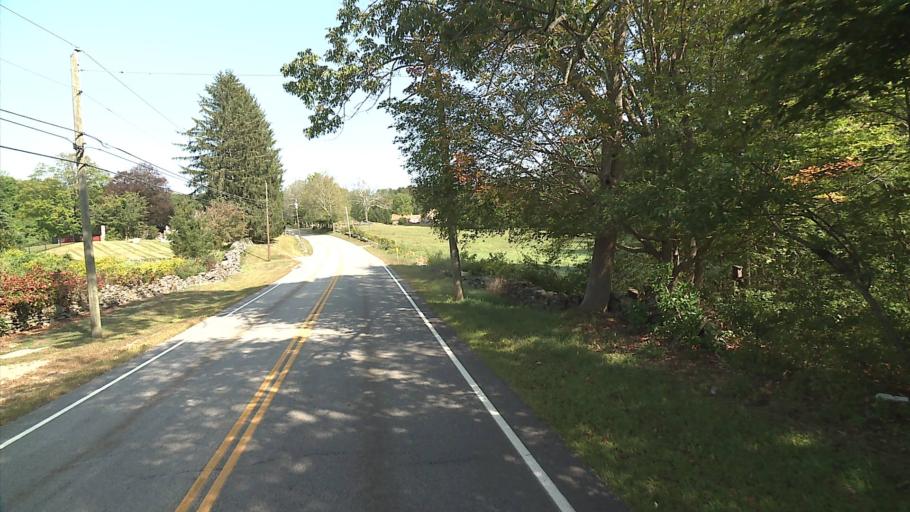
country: US
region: Connecticut
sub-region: Windham County
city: Plainfield Village
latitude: 41.7125
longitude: -71.9701
